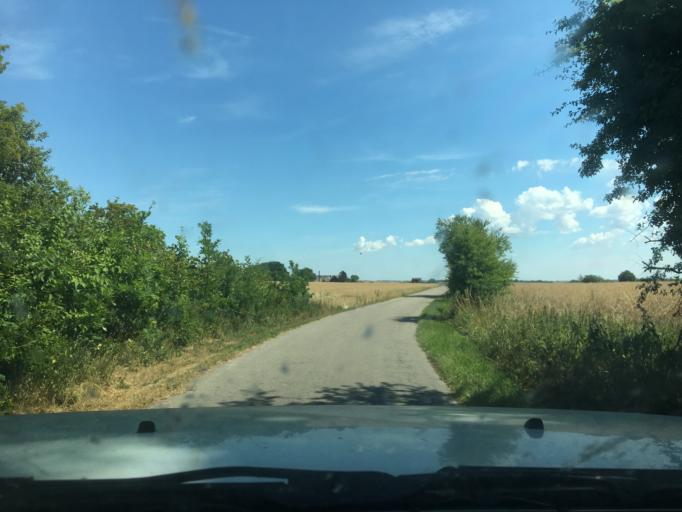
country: DK
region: Central Jutland
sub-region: Randers Kommune
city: Assentoft
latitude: 56.3499
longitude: 10.1826
